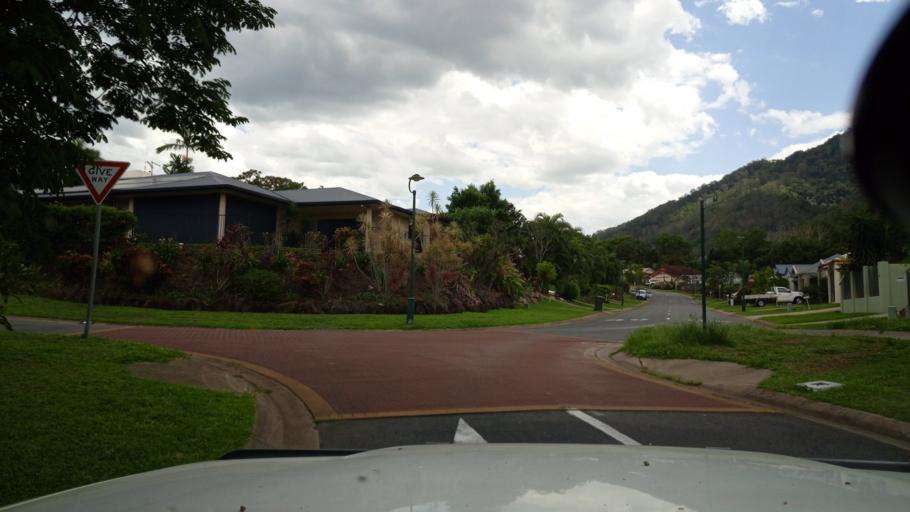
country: AU
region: Queensland
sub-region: Cairns
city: Redlynch
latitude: -16.9101
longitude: 145.7175
